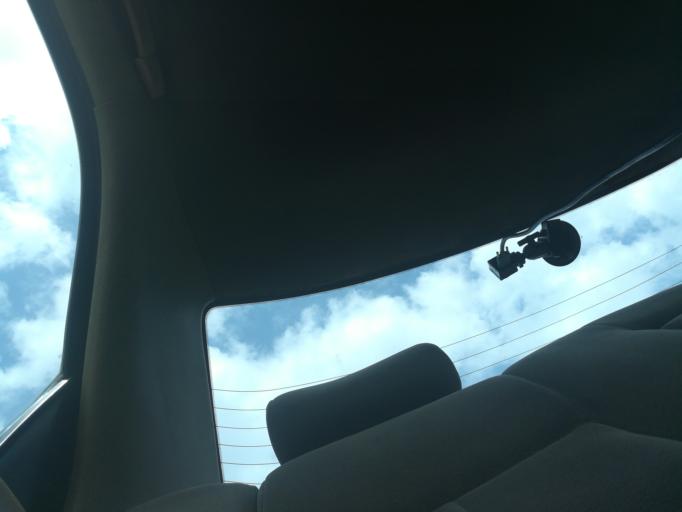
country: NG
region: Lagos
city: Ikorodu
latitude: 6.6631
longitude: 3.6137
